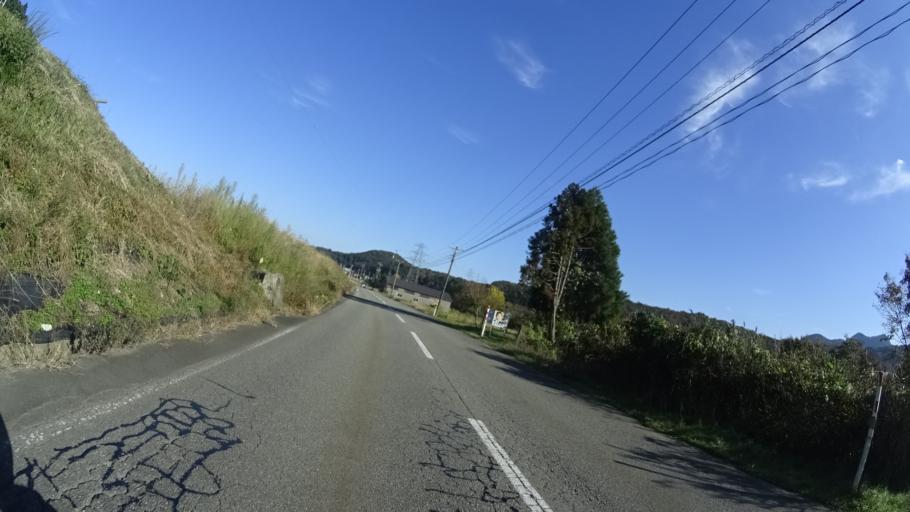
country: JP
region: Ishikawa
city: Komatsu
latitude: 36.2632
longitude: 136.3931
